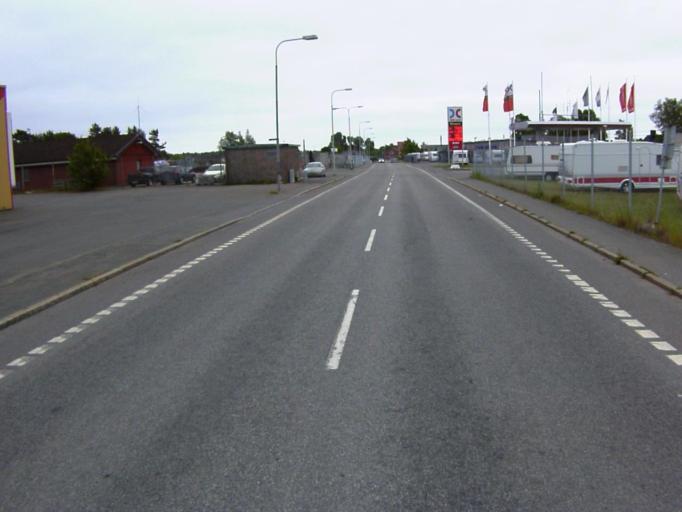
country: SE
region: Skane
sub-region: Kristianstads Kommun
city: Ahus
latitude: 55.9333
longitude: 14.2913
